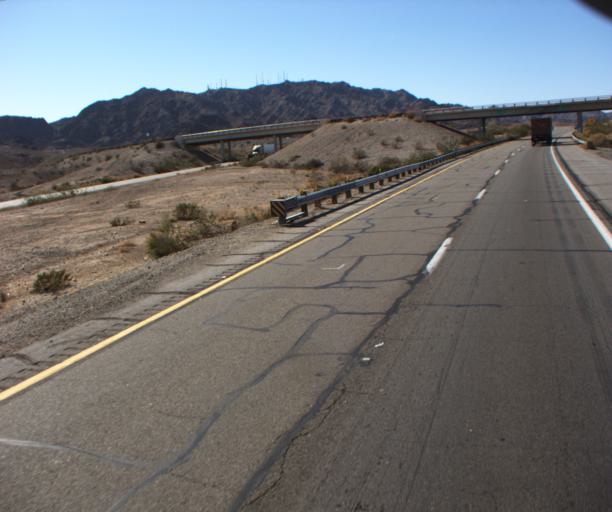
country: US
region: Arizona
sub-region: Yuma County
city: Fortuna Foothills
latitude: 32.6719
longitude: -114.3020
